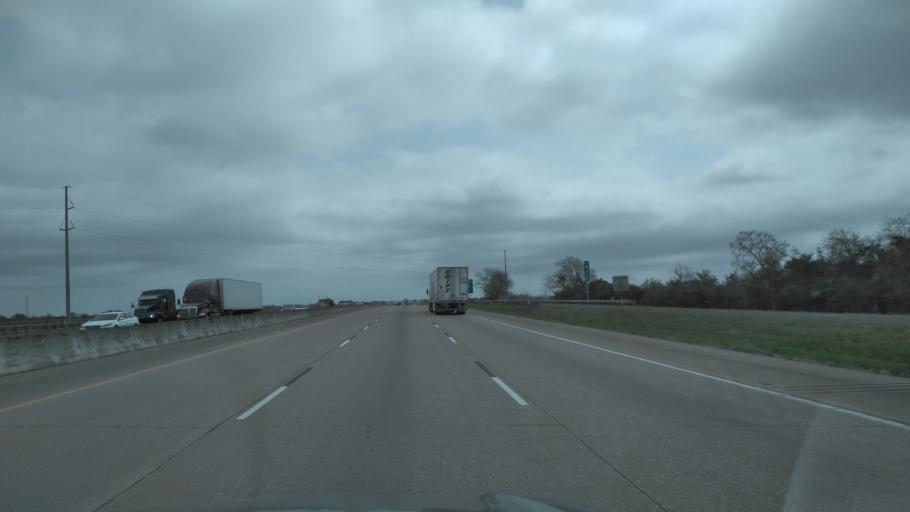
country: US
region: Texas
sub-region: Chambers County
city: Winnie
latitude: 29.8314
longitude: -94.4980
